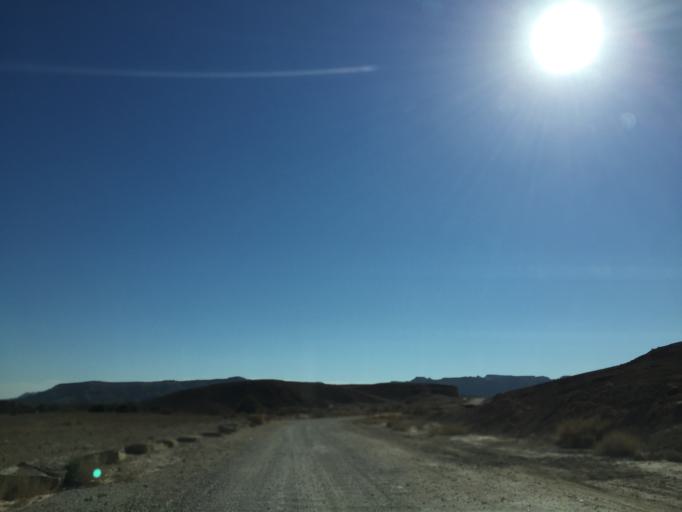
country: IL
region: Southern District
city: Mitzpe Ramon
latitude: 30.6227
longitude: 34.9211
